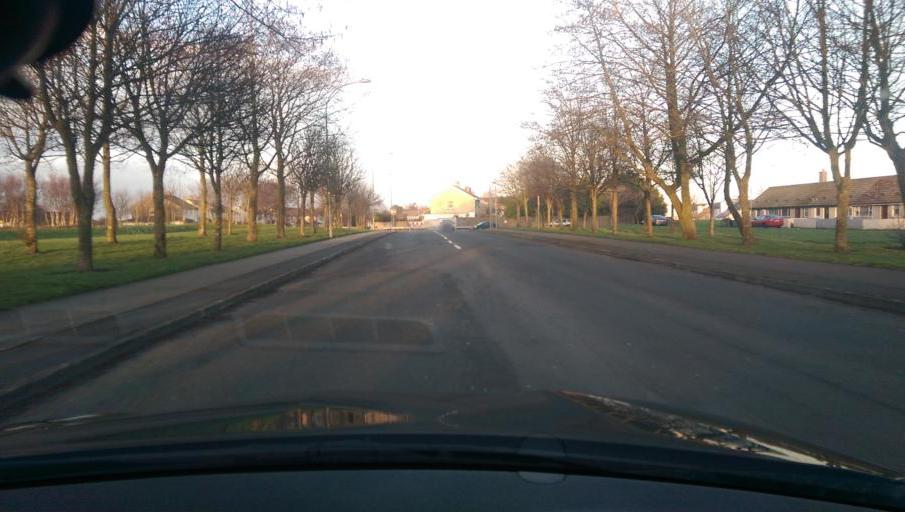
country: IE
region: Connaught
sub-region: County Galway
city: Gaillimh
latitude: 53.2817
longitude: -9.0734
